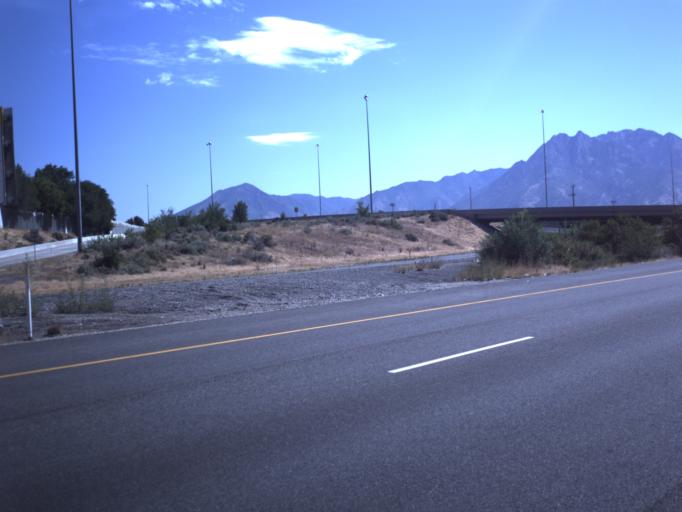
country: US
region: Utah
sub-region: Salt Lake County
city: Midvale
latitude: 40.6358
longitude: -111.9093
